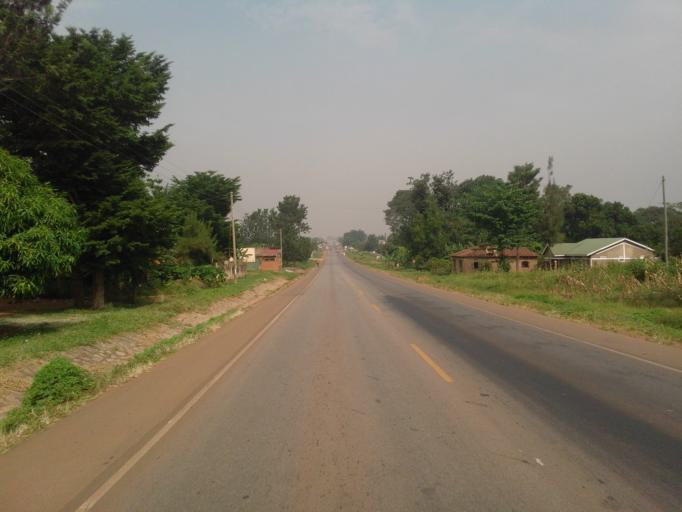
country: UG
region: Eastern Region
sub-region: Bugiri District
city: Bugiri
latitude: 0.5607
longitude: 33.7592
